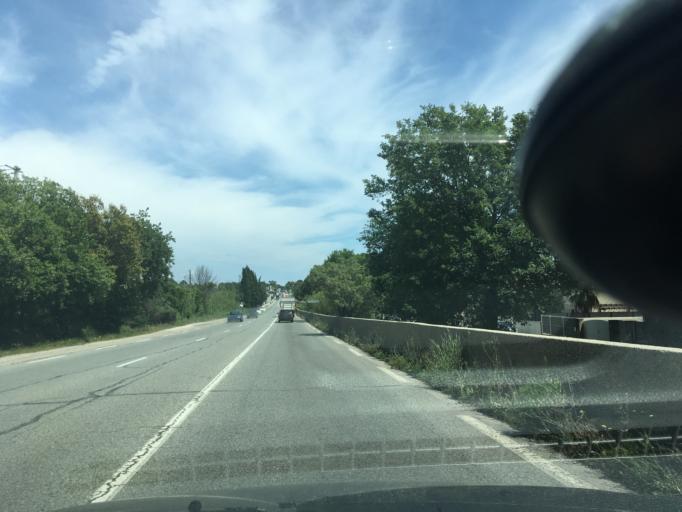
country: FR
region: Provence-Alpes-Cote d'Azur
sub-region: Departement du Var
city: Puget-sur-Argens
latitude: 43.4584
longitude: 6.6743
